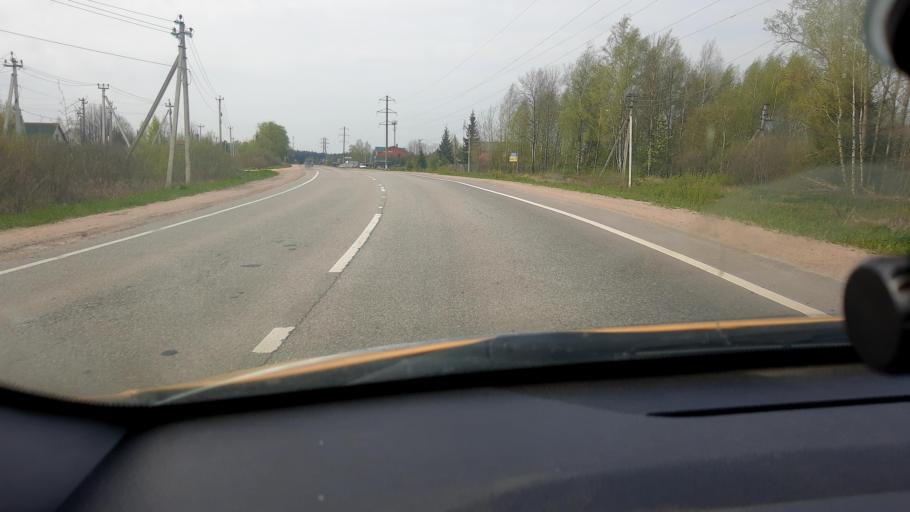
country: RU
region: Moskovskaya
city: Rumyantsevo
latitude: 55.9104
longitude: 36.5899
